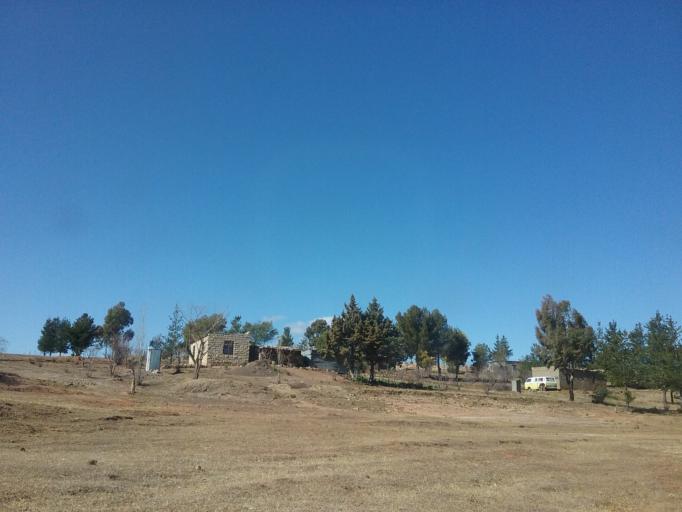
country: LS
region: Maseru
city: Maseru
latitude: -29.4672
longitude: 27.5784
